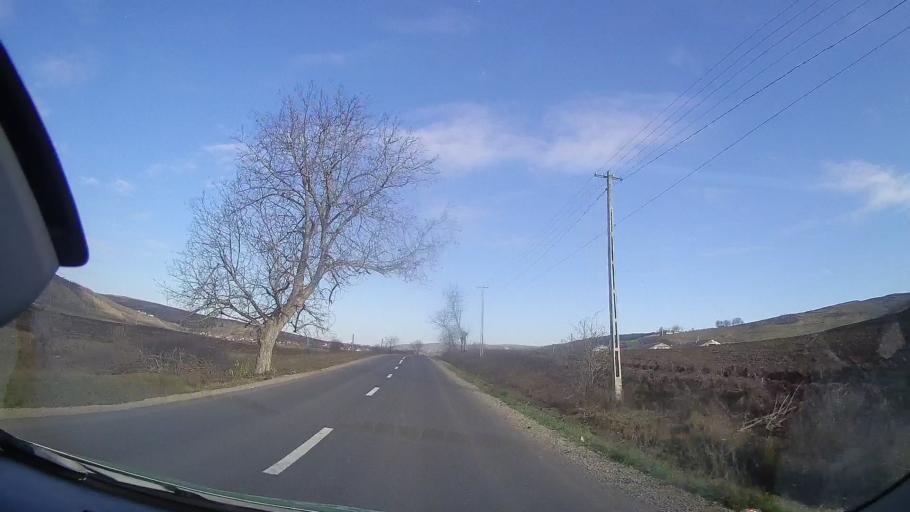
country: RO
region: Mures
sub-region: Comuna Zau De Campie
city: Zau de Campie
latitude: 46.5922
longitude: 24.1071
